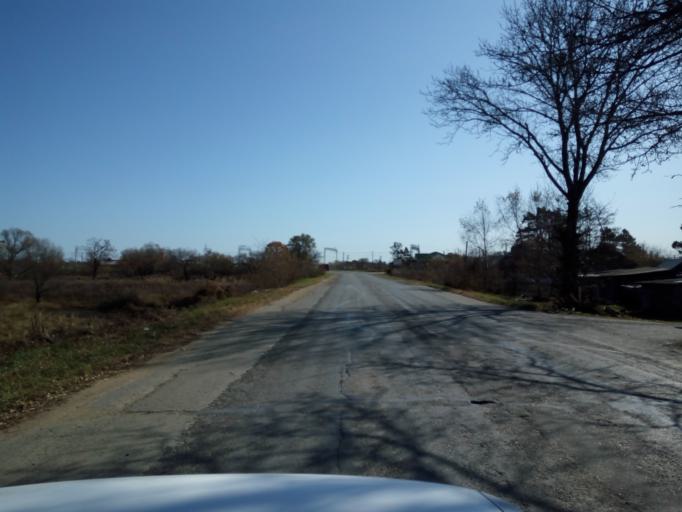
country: RU
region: Primorskiy
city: Dal'nerechensk
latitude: 45.9133
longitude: 133.7911
